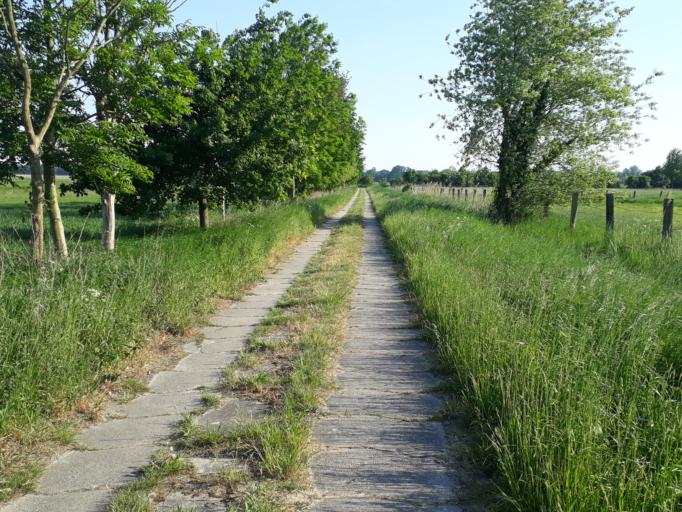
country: DE
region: Brandenburg
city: Potsdam
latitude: 52.4586
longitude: 13.0073
